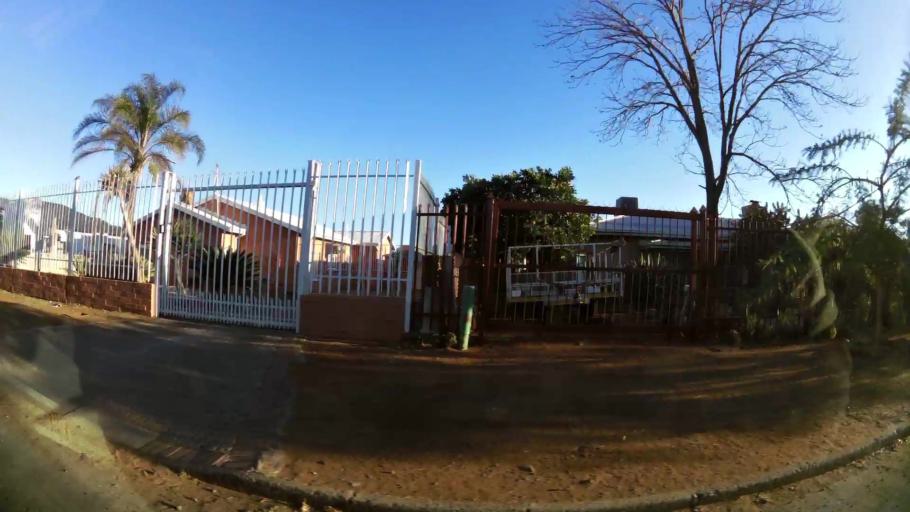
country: ZA
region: Northern Cape
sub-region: Frances Baard District Municipality
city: Kimberley
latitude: -28.7533
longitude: 24.7397
